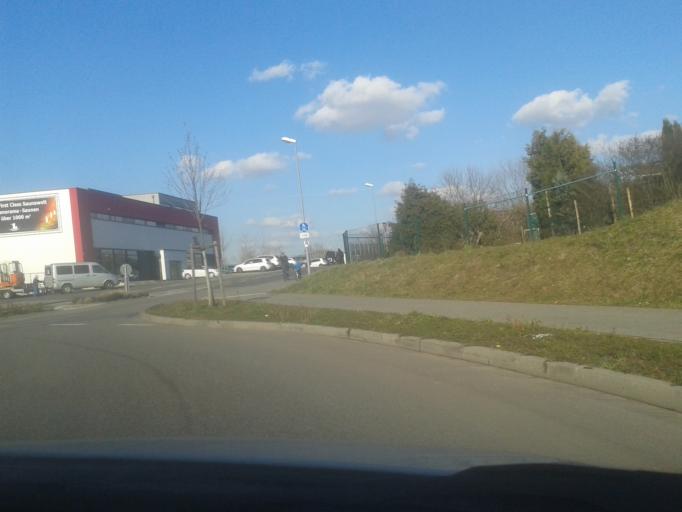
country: DE
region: Rheinland-Pfalz
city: Nieder-Ingelheim
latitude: 49.9810
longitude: 8.0630
